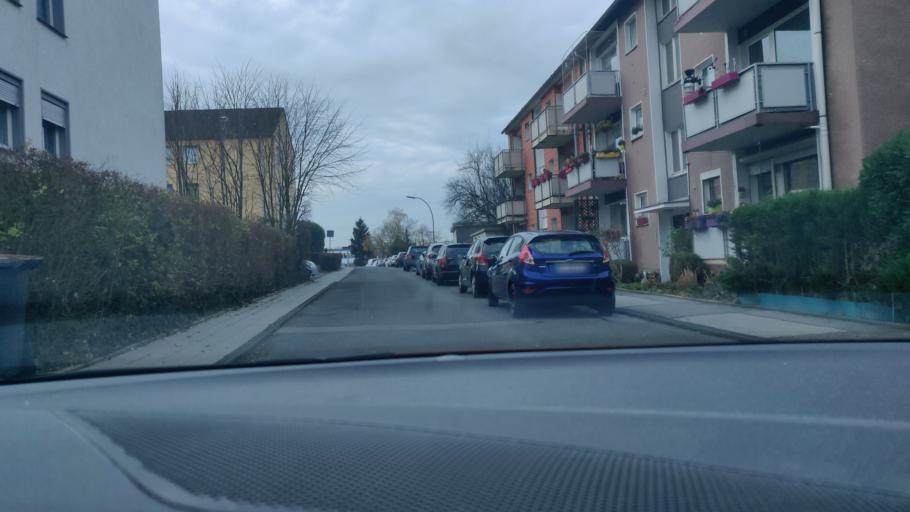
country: DE
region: North Rhine-Westphalia
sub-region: Regierungsbezirk Dusseldorf
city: Velbert
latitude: 51.3345
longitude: 7.0186
